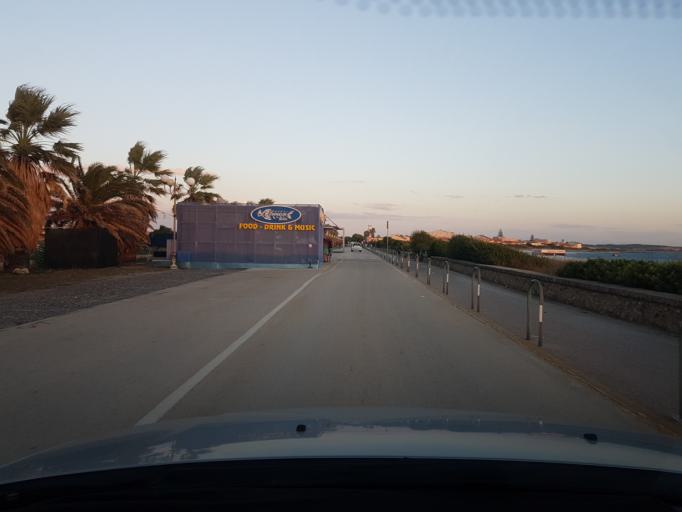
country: IT
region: Sardinia
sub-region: Provincia di Oristano
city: Riola Sardo
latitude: 40.0307
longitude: 8.4052
